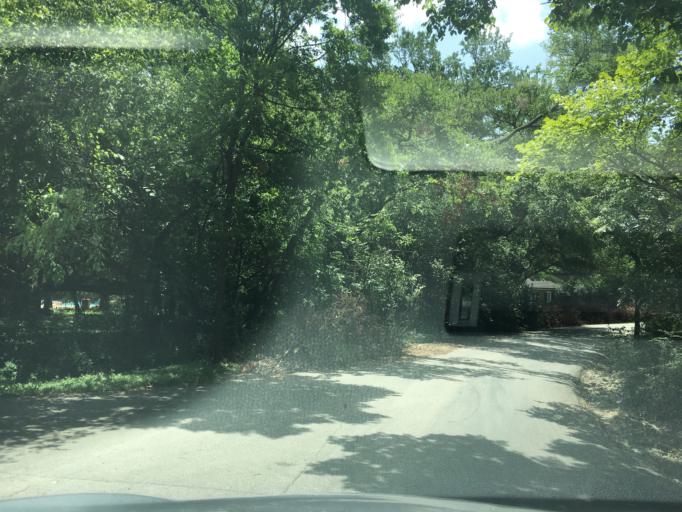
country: US
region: Texas
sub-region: Dallas County
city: University Park
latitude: 32.9055
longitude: -96.7899
